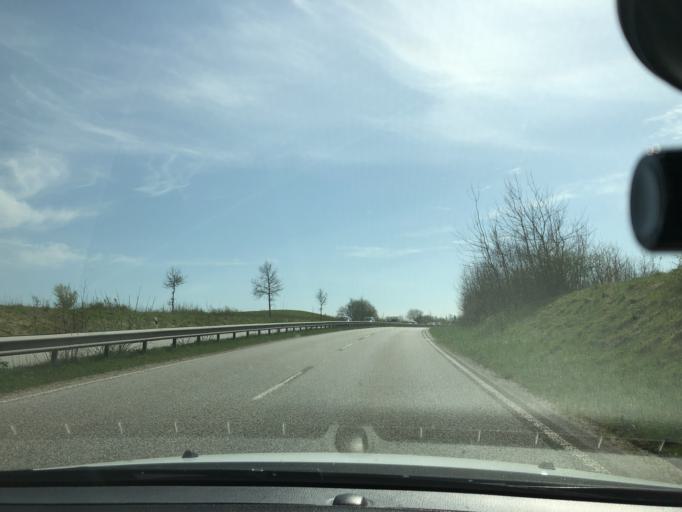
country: DE
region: Schleswig-Holstein
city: Tastrup
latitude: 54.7689
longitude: 9.4606
